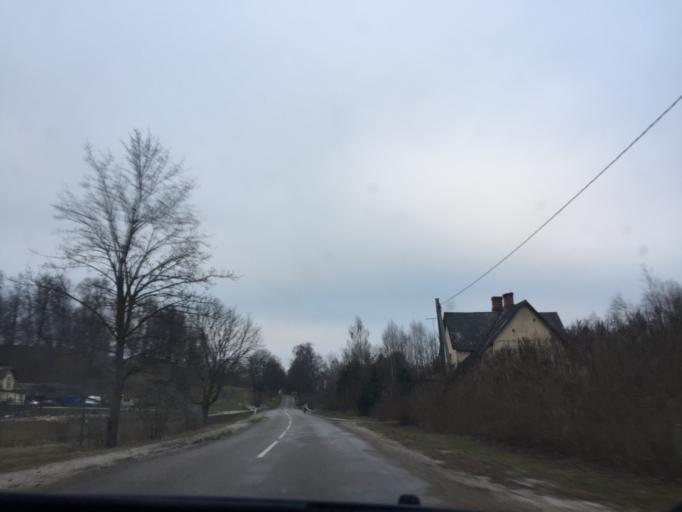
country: LV
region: Raunas
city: Rauna
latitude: 57.3277
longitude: 25.6025
